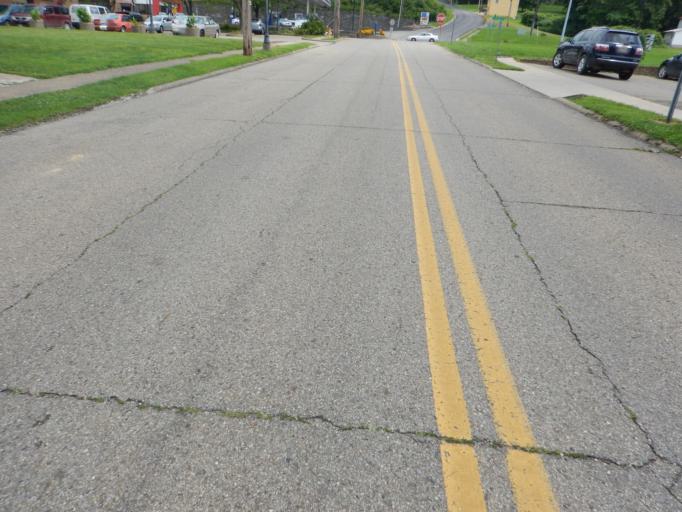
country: US
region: Ohio
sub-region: Muskingum County
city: Zanesville
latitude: 39.9434
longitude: -82.0021
